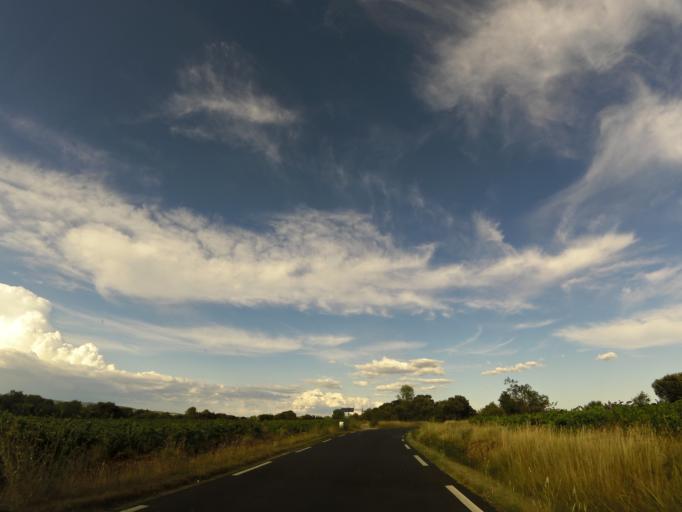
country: FR
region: Languedoc-Roussillon
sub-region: Departement de l'Herault
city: Boisseron
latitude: 43.7807
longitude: 4.0477
